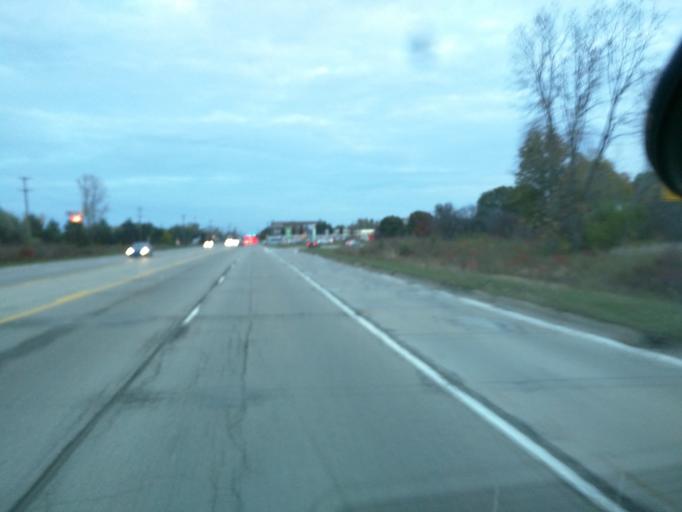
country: US
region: Michigan
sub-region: Eaton County
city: Waverly
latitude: 42.7220
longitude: -84.6029
